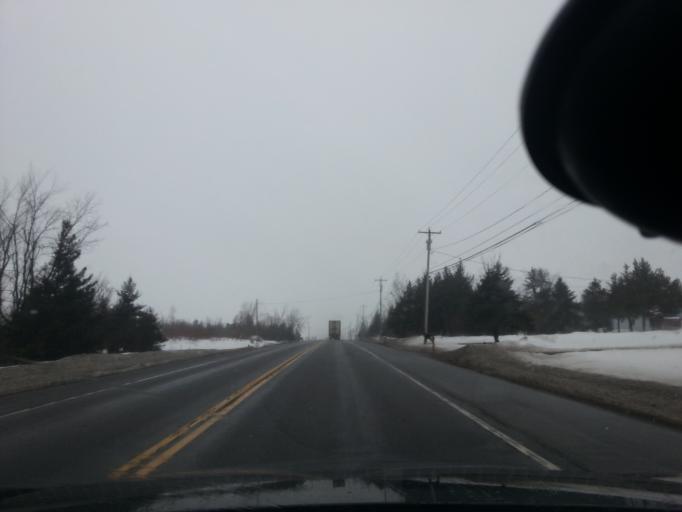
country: US
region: New York
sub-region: Jefferson County
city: Philadelphia
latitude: 44.1184
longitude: -75.7499
